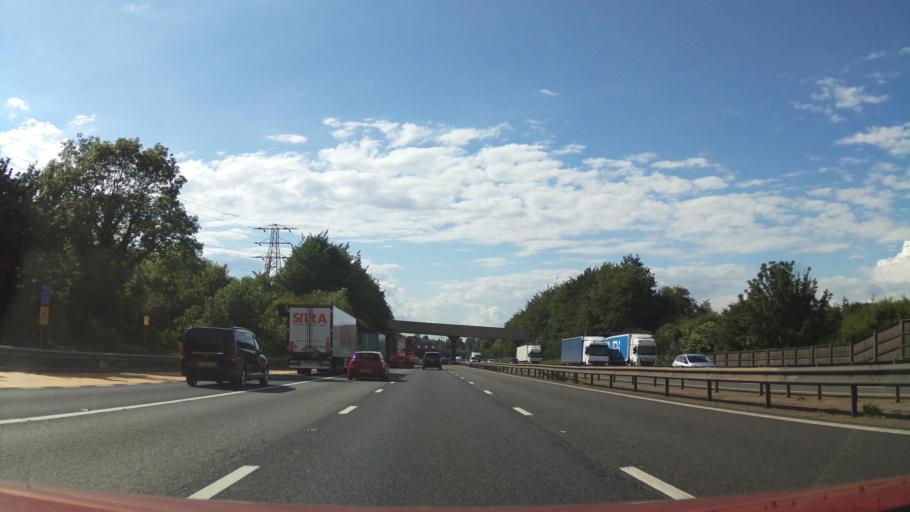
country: GB
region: England
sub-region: Central Bedfordshire
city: Caddington
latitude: 51.8841
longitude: -0.4603
